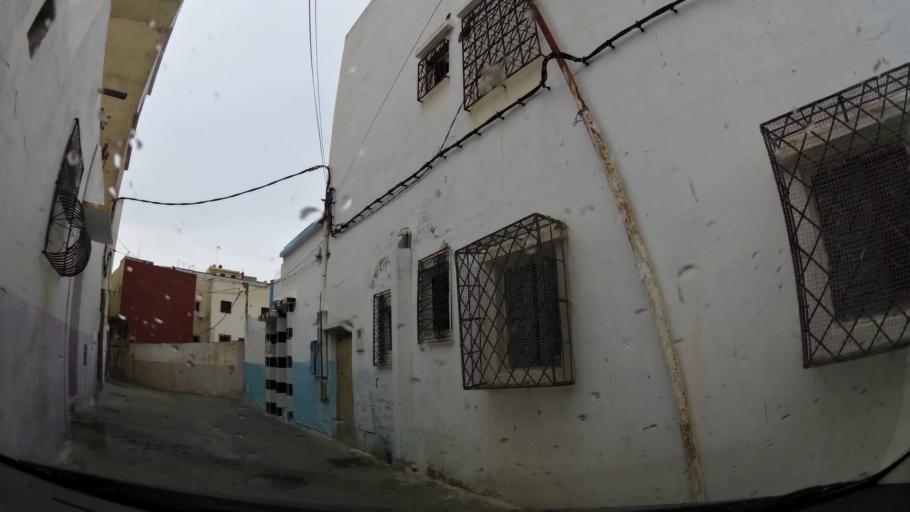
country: MA
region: Tanger-Tetouan
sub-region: Tetouan
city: Martil
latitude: 35.6218
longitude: -5.2774
